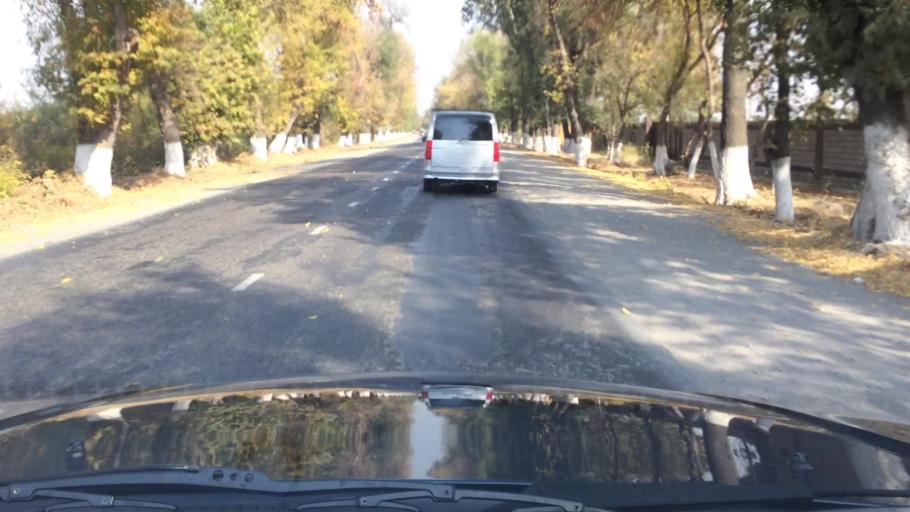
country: KG
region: Chuy
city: Lebedinovka
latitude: 42.9245
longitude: 74.6903
